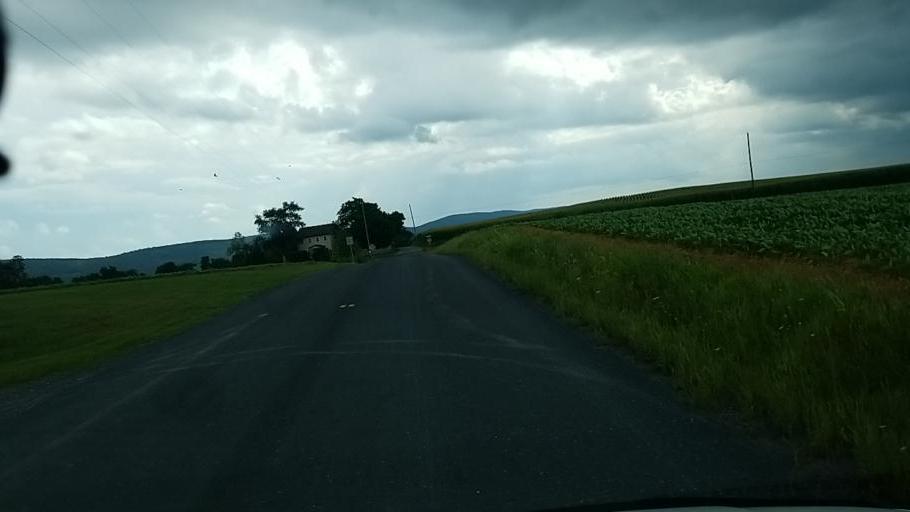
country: US
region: Pennsylvania
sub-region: Dauphin County
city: Elizabethville
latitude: 40.5727
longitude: -76.8352
